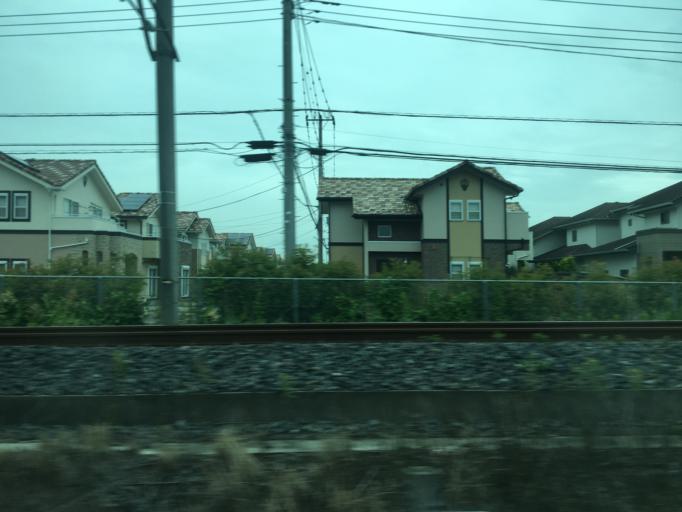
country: JP
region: Saitama
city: Kukichuo
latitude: 36.0974
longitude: 139.6789
